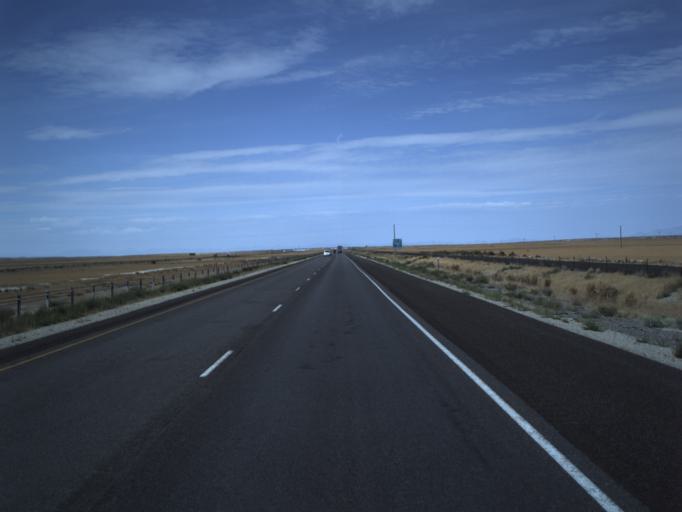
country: US
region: Utah
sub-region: Tooele County
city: Grantsville
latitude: 40.7270
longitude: -113.2306
